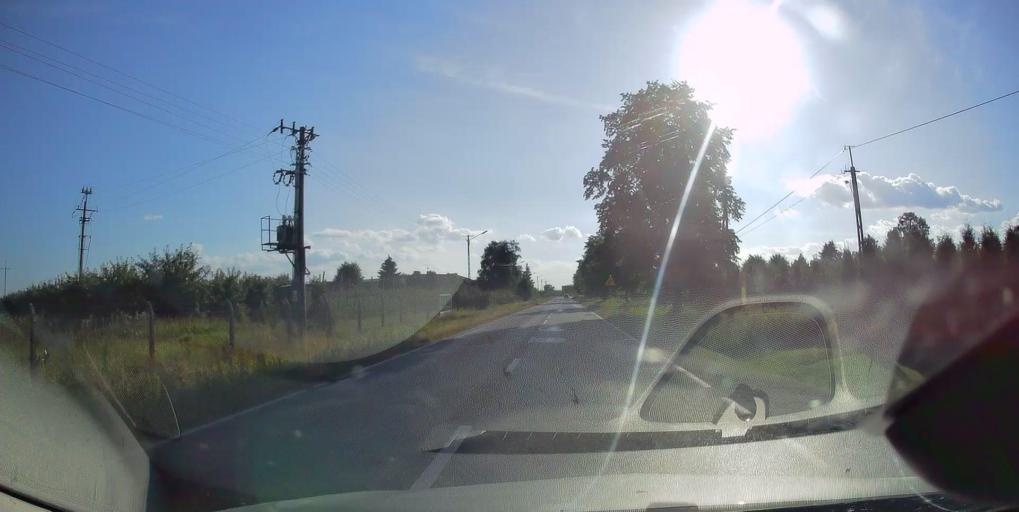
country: PL
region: Masovian Voivodeship
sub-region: Powiat grojecki
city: Belsk Duzy
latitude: 51.8137
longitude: 20.7540
